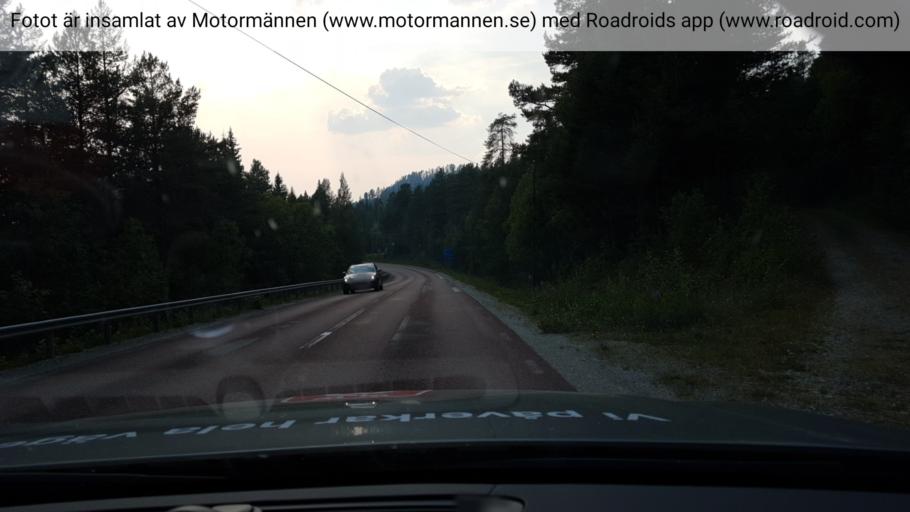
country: NO
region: Hedmark
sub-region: Engerdal
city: Engerdal
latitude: 62.4408
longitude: 12.7211
